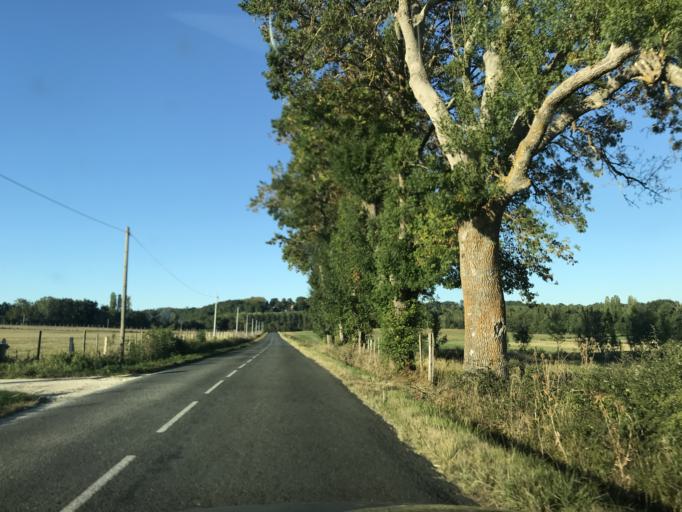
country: FR
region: Aquitaine
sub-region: Departement de la Gironde
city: Rauzan
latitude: 44.7675
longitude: -0.0639
